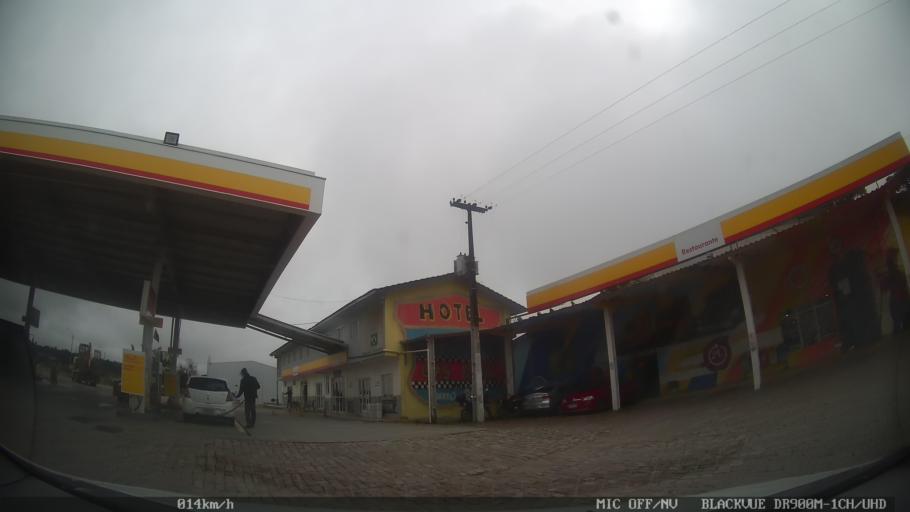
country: BR
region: Parana
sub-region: Sao Jose Dos Pinhais
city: Sao Jose dos Pinhais
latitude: -25.8242
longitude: -49.1233
